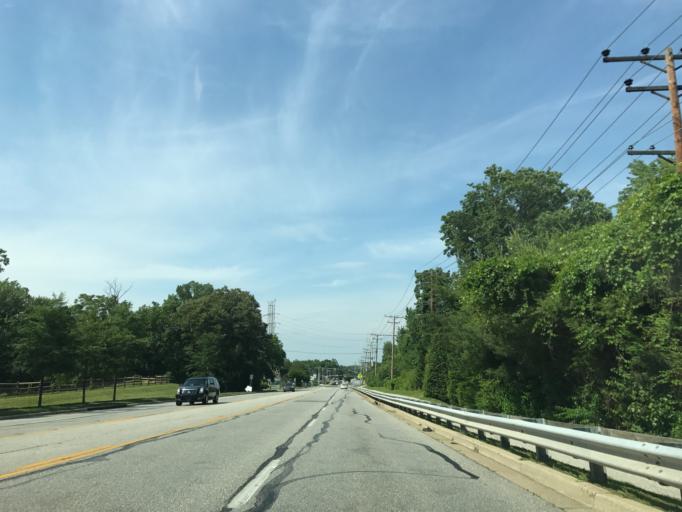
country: US
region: Maryland
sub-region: Anne Arundel County
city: Odenton
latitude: 39.0807
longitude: -76.7015
